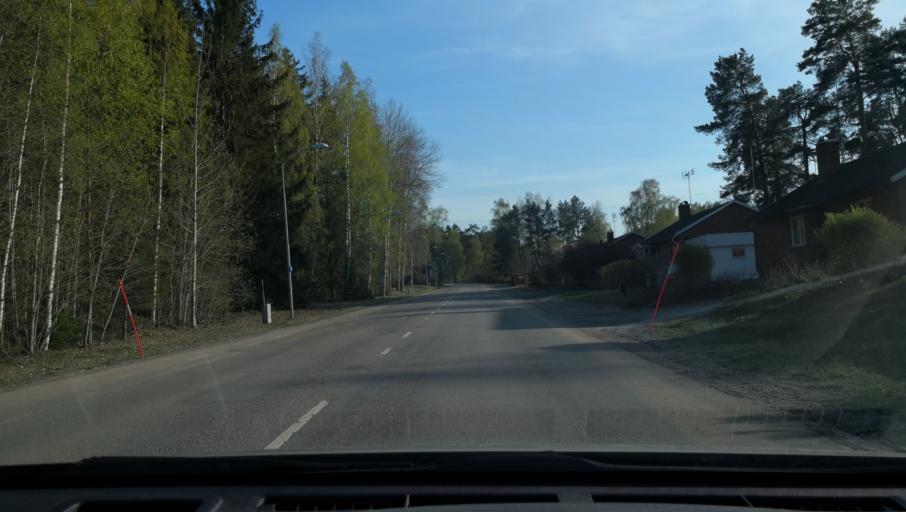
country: SE
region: Uppsala
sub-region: Heby Kommun
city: Tarnsjo
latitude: 60.1668
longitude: 16.9388
